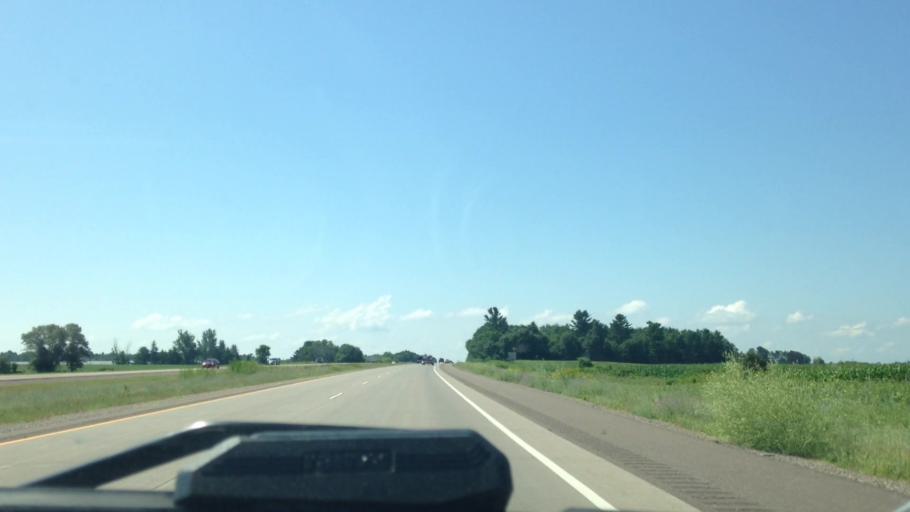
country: US
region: Wisconsin
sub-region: Barron County
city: Cameron
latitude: 45.4429
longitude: -91.7599
